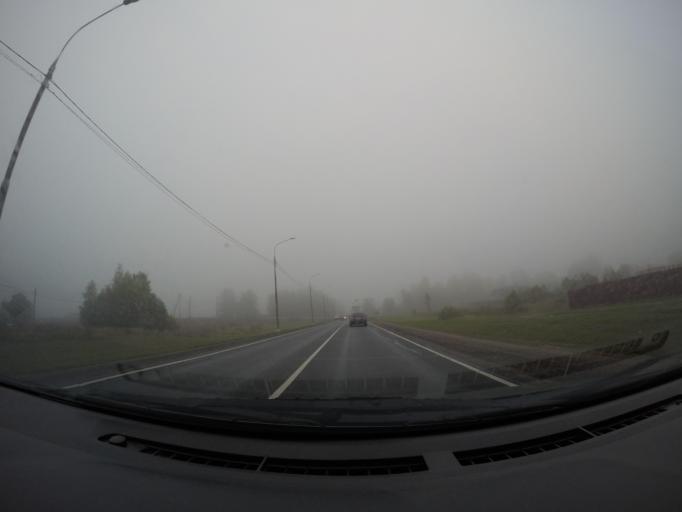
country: RU
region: Moskovskaya
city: Ruza
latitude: 55.7717
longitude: 36.2651
